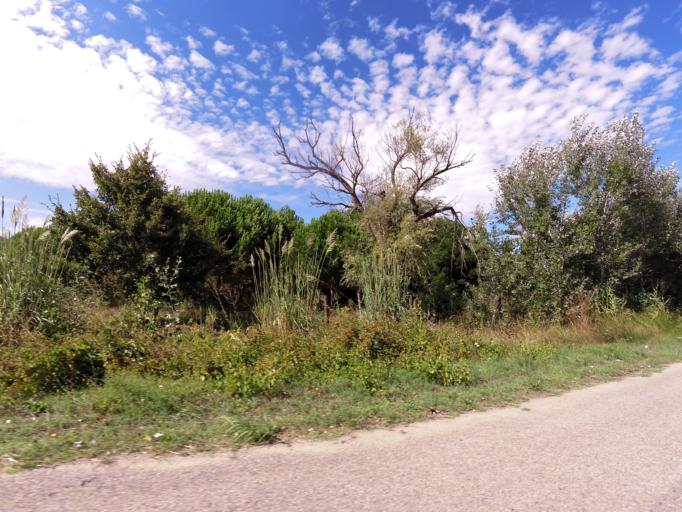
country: FR
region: Languedoc-Roussillon
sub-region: Departement du Gard
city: Aigues-Mortes
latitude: 43.5750
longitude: 4.1785
